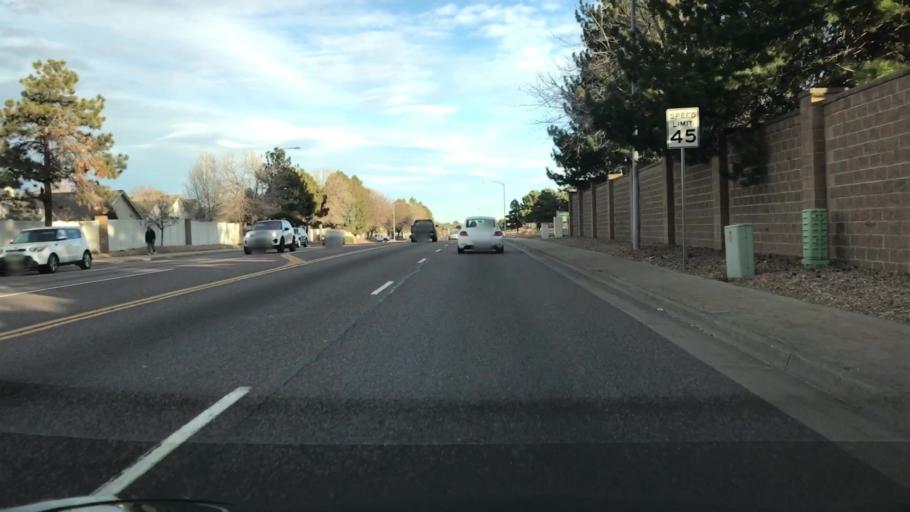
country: US
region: Colorado
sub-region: Adams County
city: Aurora
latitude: 39.6748
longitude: -104.8561
